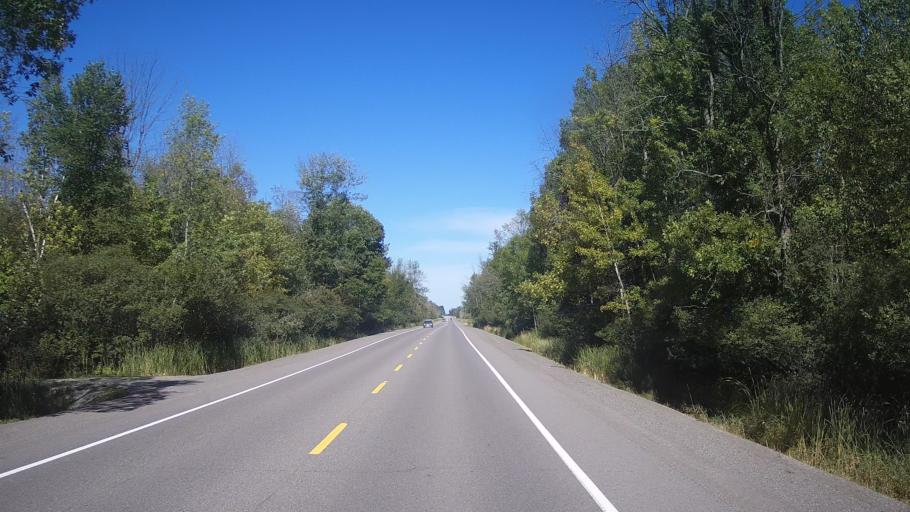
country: CA
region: Ontario
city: Bells Corners
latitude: 45.0806
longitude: -75.6522
